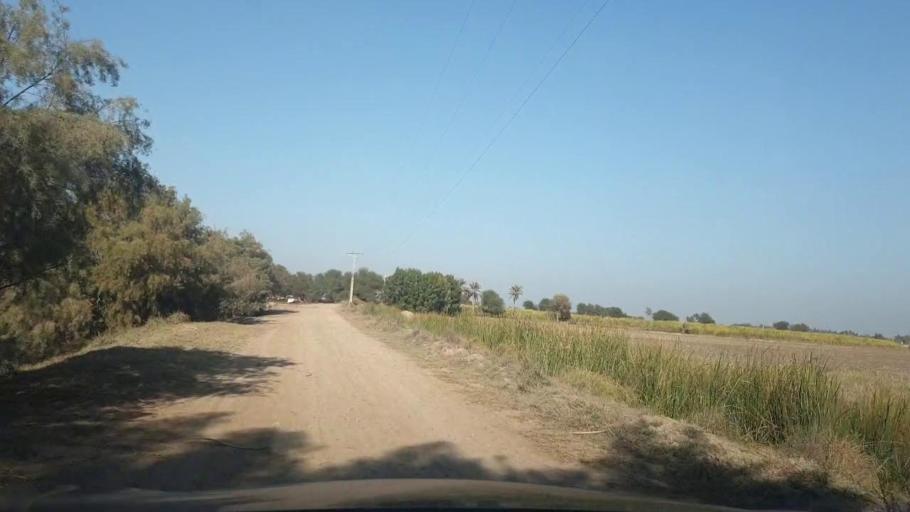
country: PK
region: Sindh
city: Mirpur Mathelo
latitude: 28.1404
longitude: 69.5967
